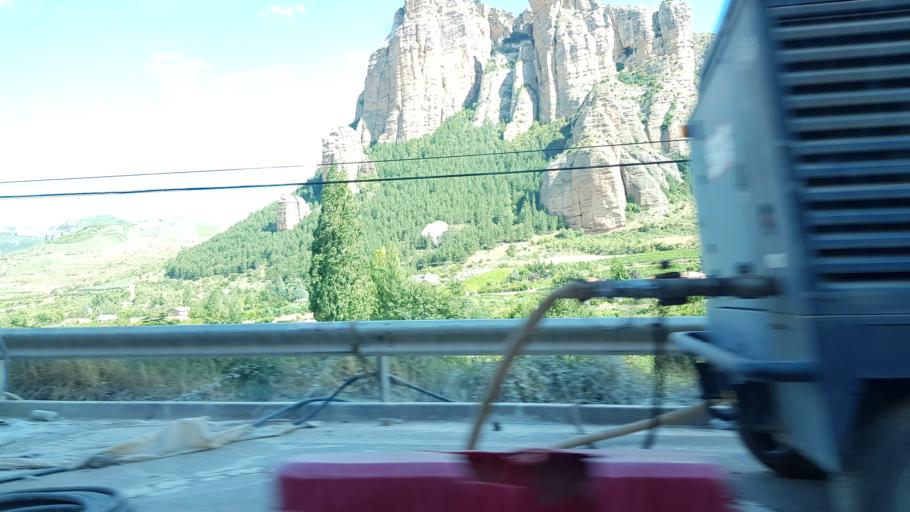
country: ES
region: La Rioja
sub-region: Provincia de La Rioja
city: Viguera
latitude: 42.3217
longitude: -2.5172
